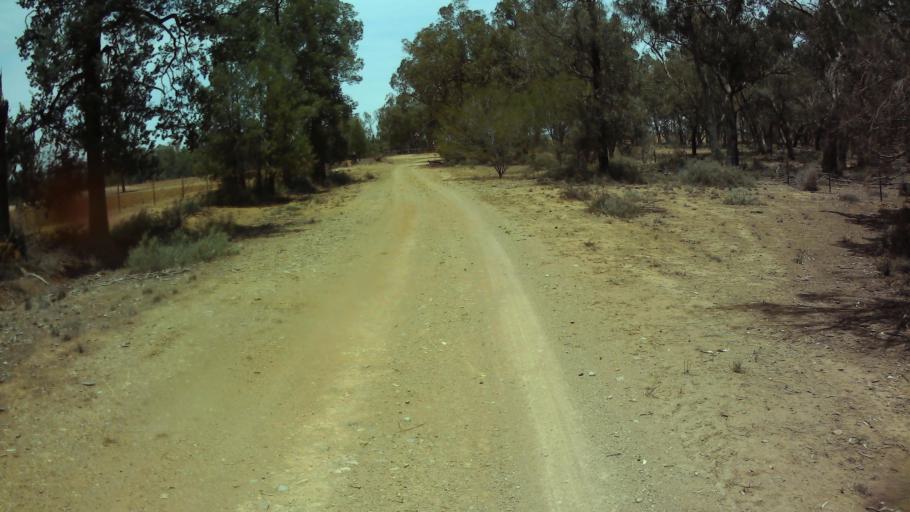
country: AU
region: New South Wales
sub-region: Weddin
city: Grenfell
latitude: -33.8440
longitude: 147.7251
